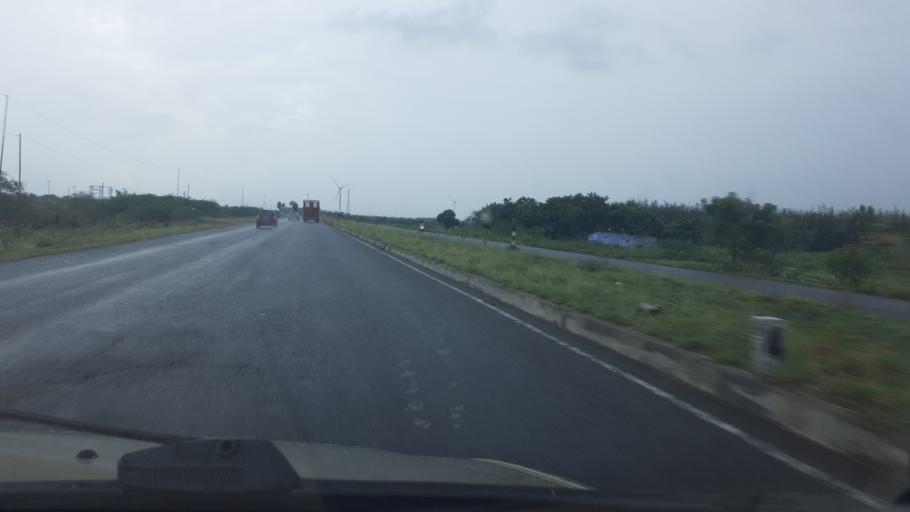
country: IN
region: Tamil Nadu
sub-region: Thoothukkudi
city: Kayattar
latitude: 9.0126
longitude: 77.7839
